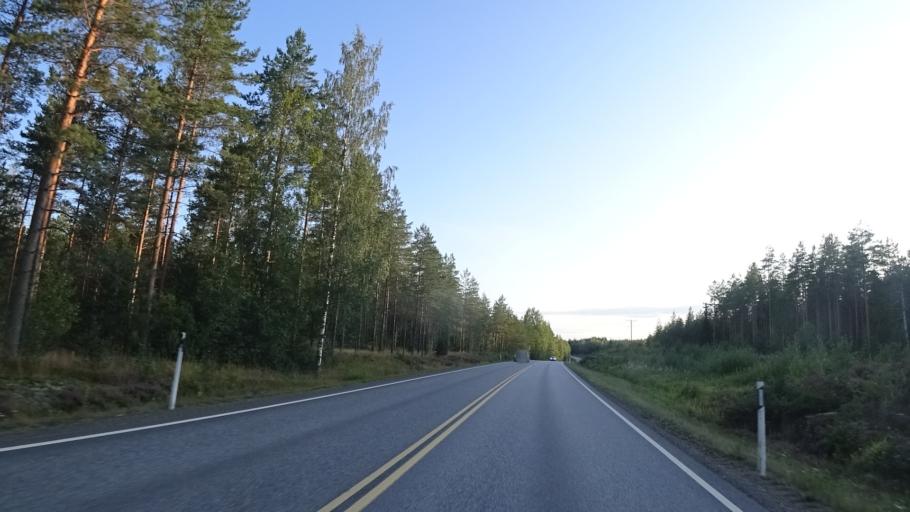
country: FI
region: South Karelia
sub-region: Lappeenranta
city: Ylaemaa
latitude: 60.8362
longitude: 28.1094
